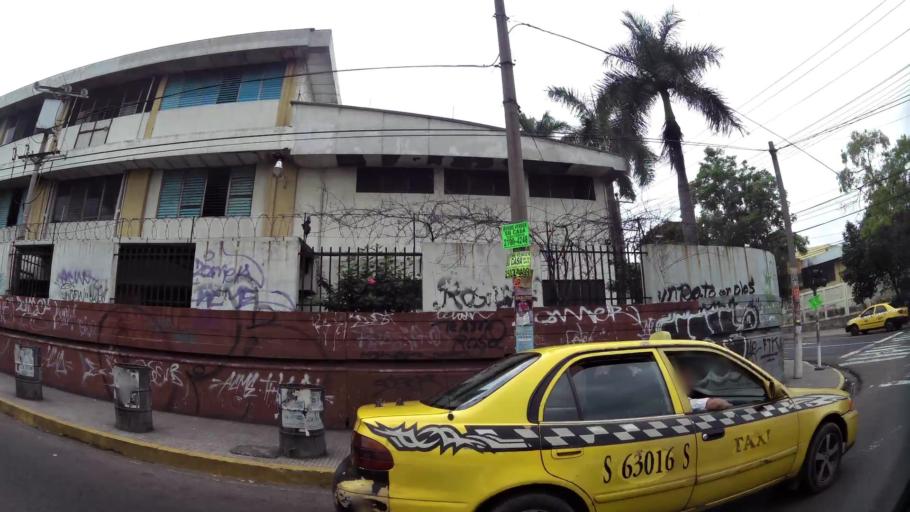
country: SV
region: San Salvador
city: San Salvador
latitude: 13.7013
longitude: -89.2046
